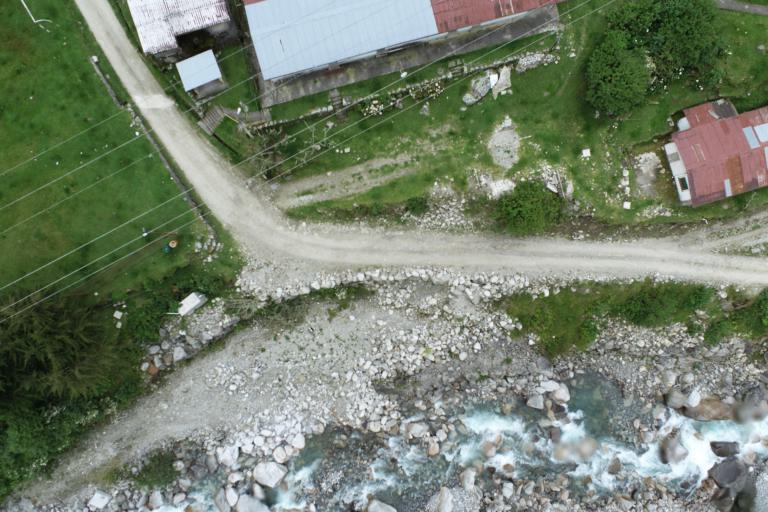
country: BO
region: La Paz
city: Coroico
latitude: -16.1231
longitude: -68.0884
